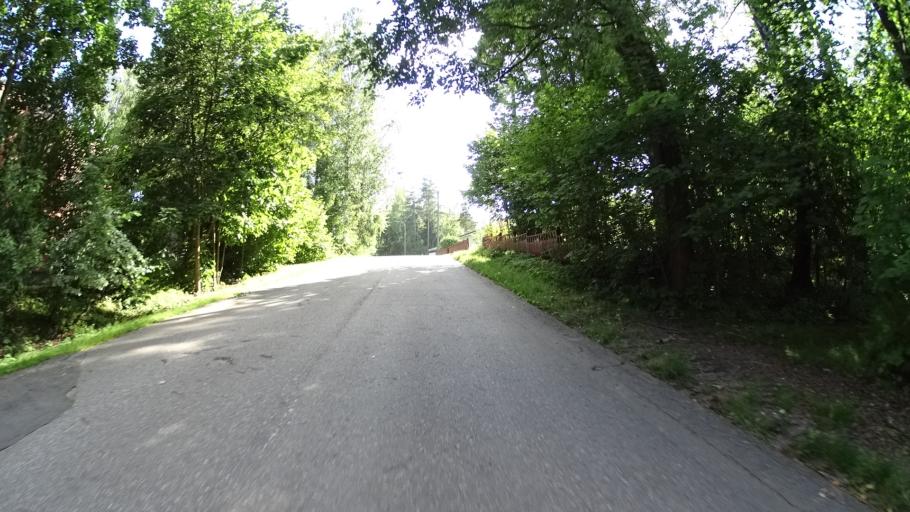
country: FI
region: Uusimaa
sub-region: Helsinki
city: Kilo
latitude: 60.2583
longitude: 24.7768
